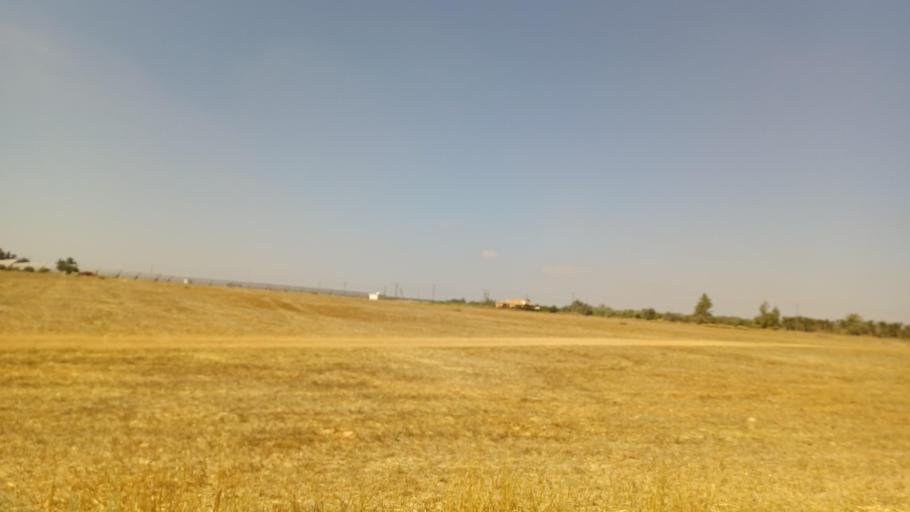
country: CY
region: Ammochostos
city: Acheritou
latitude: 35.0673
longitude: 33.8638
